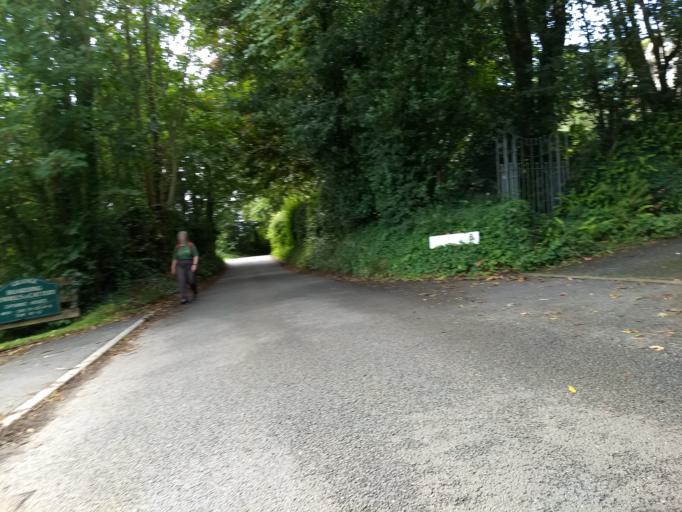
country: GB
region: England
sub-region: Isle of Wight
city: Newport
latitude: 50.6857
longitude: -1.2952
